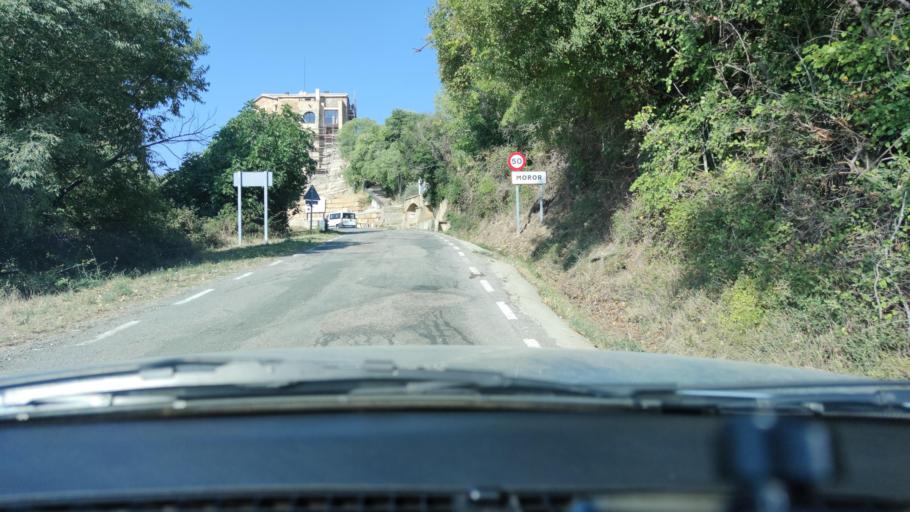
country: ES
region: Catalonia
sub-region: Provincia de Lleida
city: Llimiana
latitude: 42.0795
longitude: 0.8379
